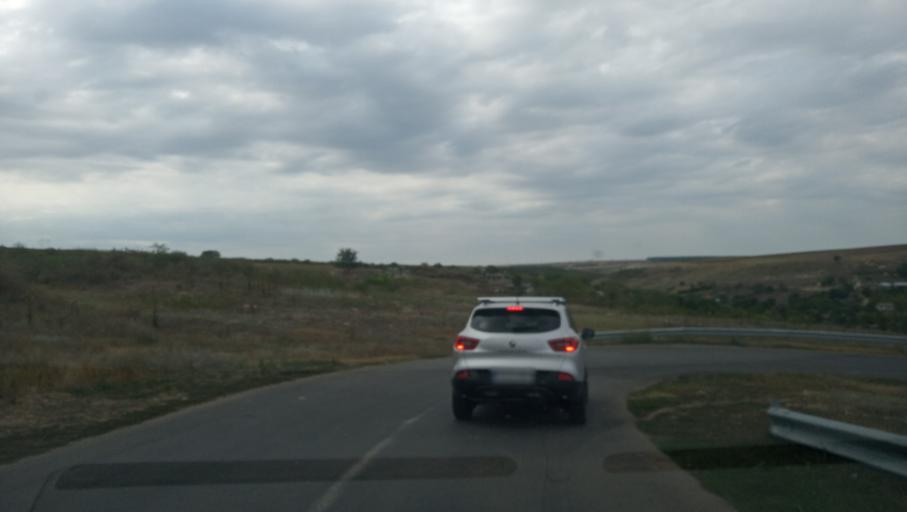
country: RO
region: Constanta
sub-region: Comuna Dumbraveni
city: Dumbraveni
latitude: 43.9891
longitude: 28.0072
